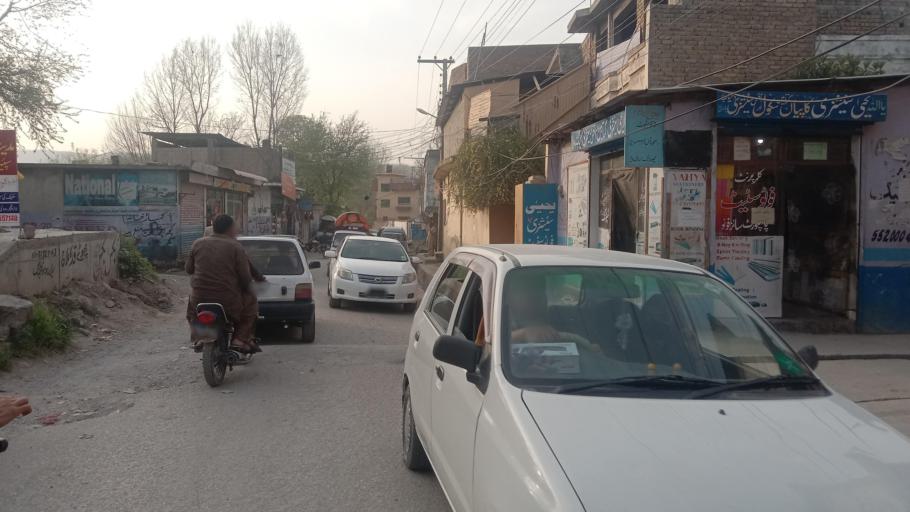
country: PK
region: Khyber Pakhtunkhwa
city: Abbottabad
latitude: 34.1743
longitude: 73.2438
